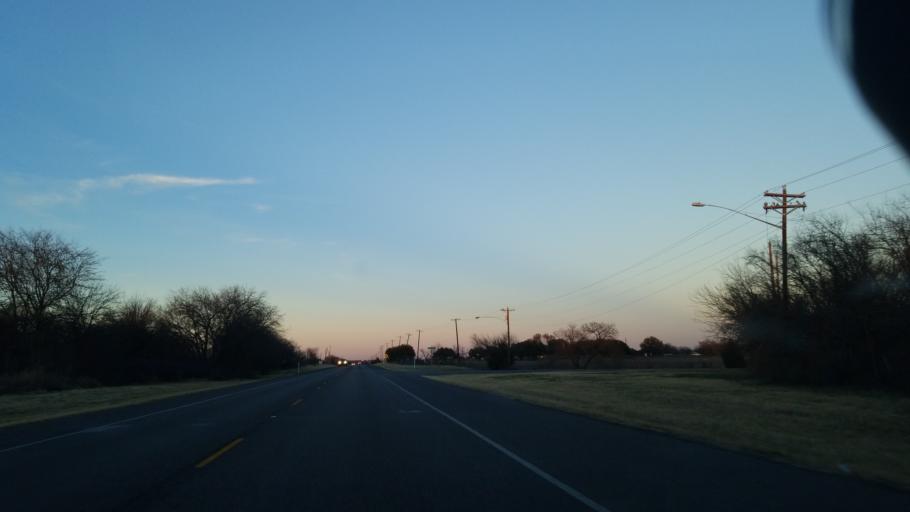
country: US
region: Texas
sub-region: Denton County
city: Argyle
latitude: 33.1468
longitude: -97.1698
